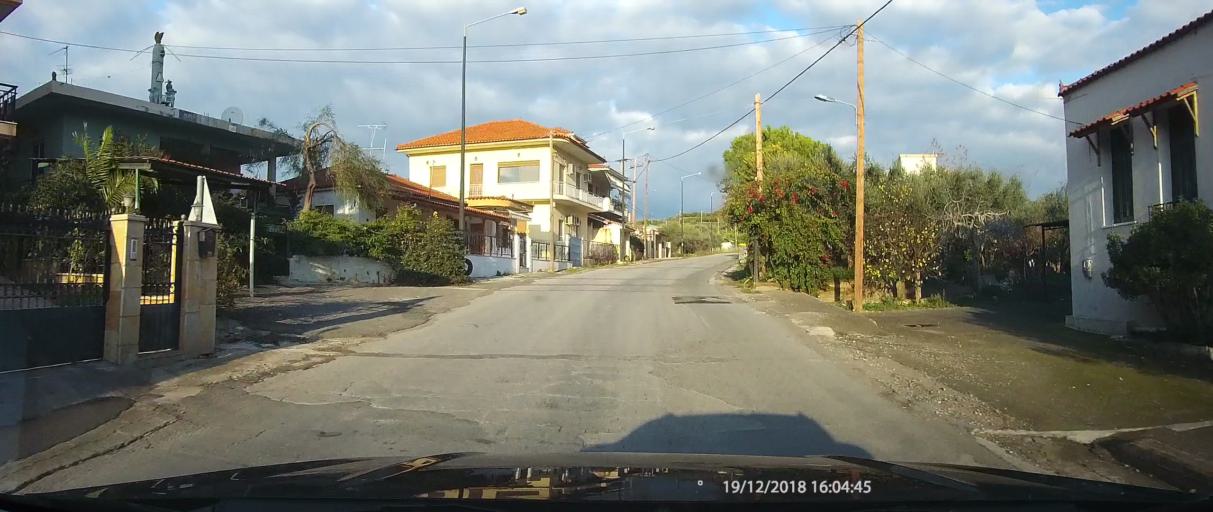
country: GR
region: Peloponnese
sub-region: Nomos Lakonias
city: Vlakhiotis
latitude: 36.8623
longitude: 22.7142
